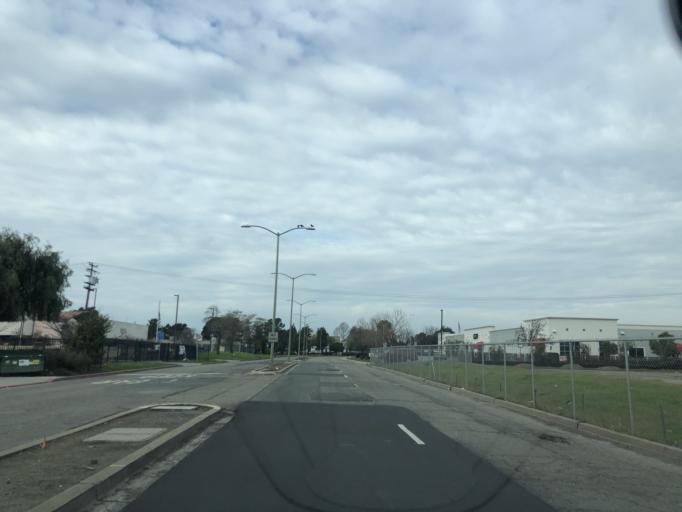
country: US
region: California
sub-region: Alameda County
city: San Leandro
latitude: 37.7302
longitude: -122.2011
